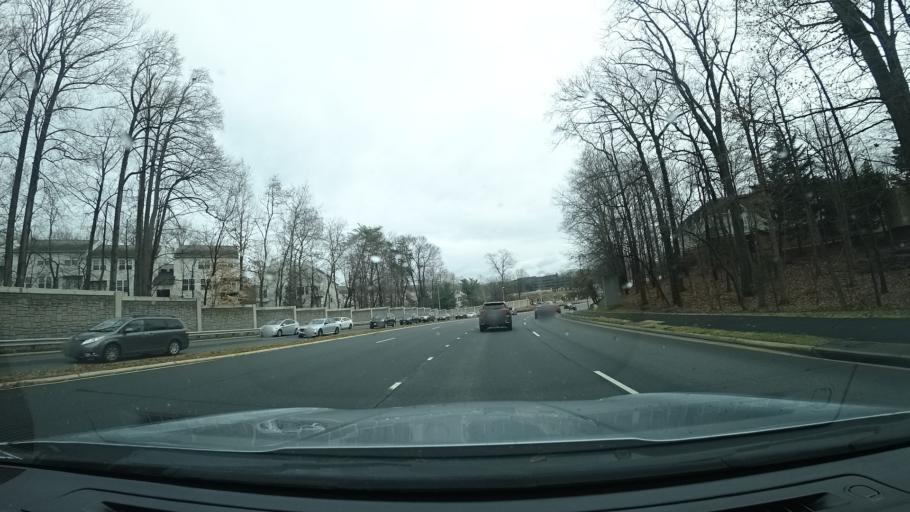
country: US
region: Virginia
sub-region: Fairfax County
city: Greenbriar
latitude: 38.8627
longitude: -77.3856
